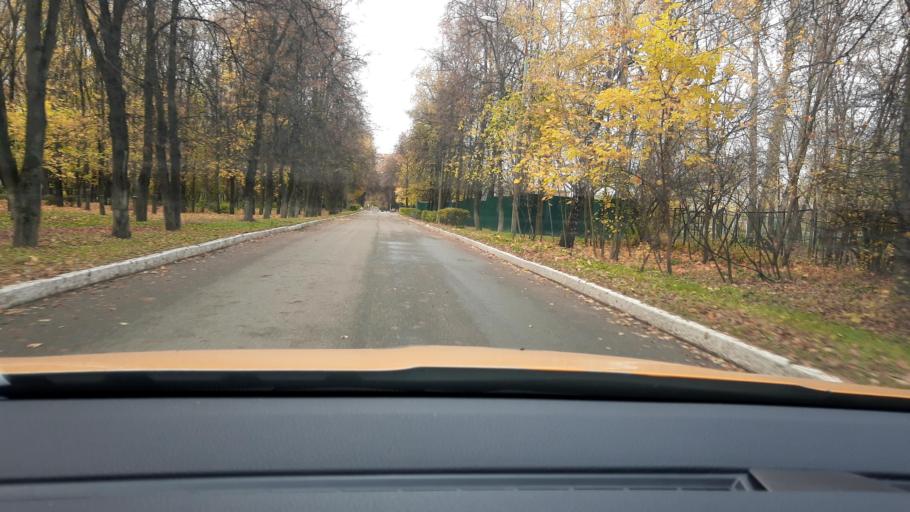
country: RU
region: Moscow
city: Kuz'minki
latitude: 55.6990
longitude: 37.7966
